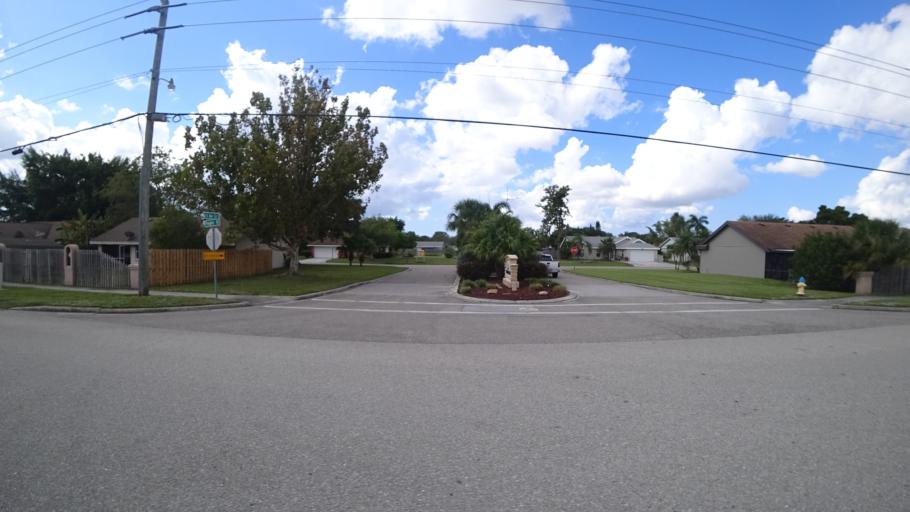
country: US
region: Florida
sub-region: Manatee County
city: Whitfield
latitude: 27.4239
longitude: -82.5177
